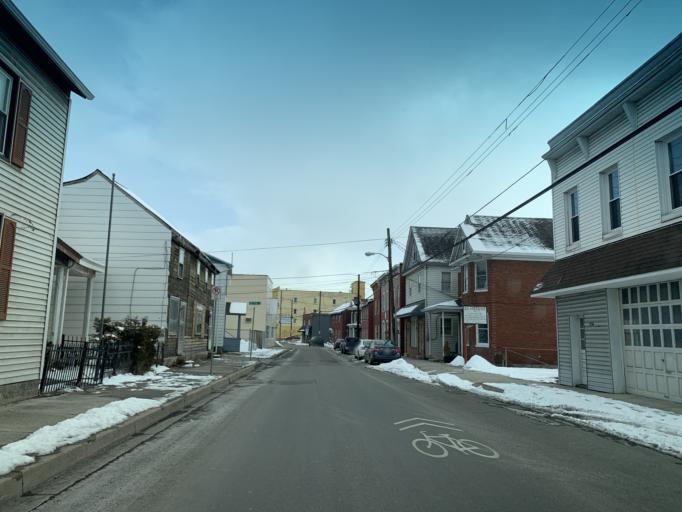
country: US
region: Maryland
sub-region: Allegany County
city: Cumberland
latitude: 39.6572
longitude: -78.7712
